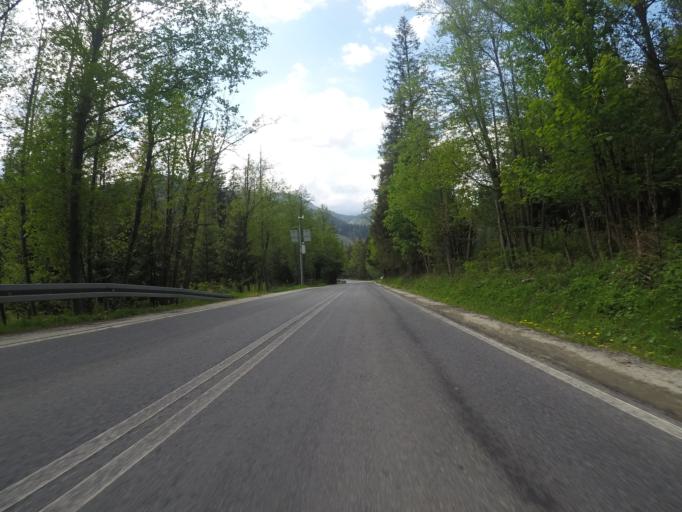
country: PL
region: Lesser Poland Voivodeship
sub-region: Powiat tatrzanski
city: Bukowina Tatrzanska
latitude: 49.2705
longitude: 20.1199
